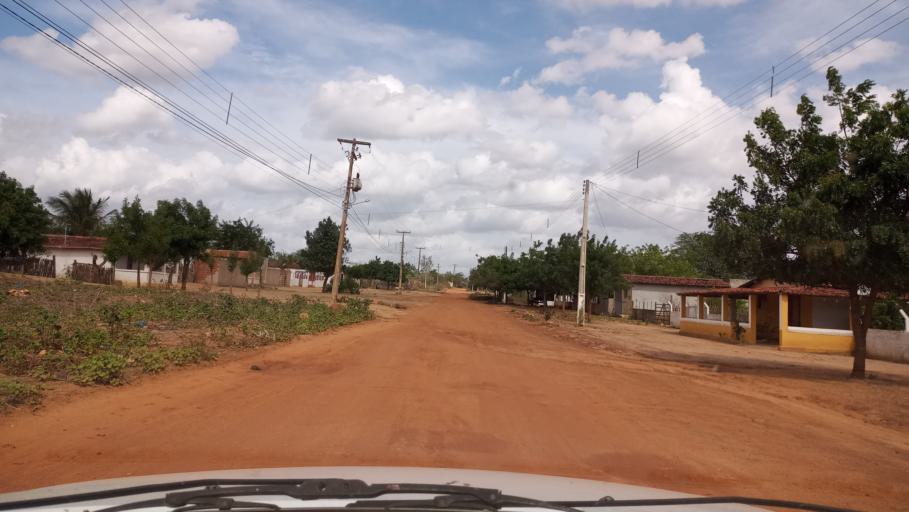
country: BR
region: Rio Grande do Norte
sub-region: Joao Camara
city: Joao Camara
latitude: -5.4696
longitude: -35.8306
